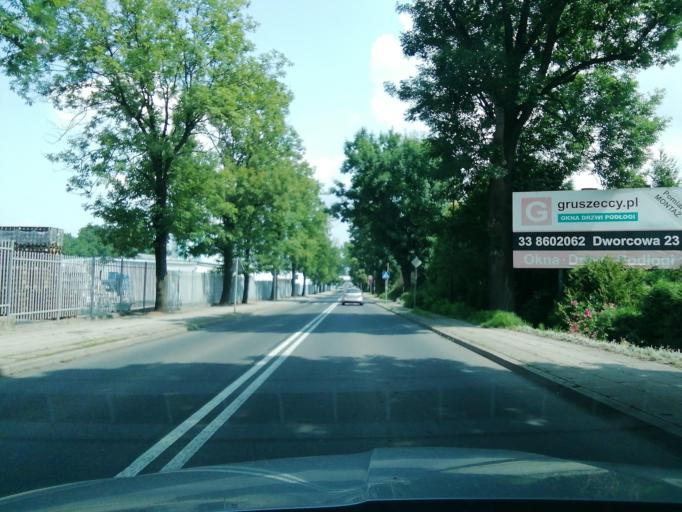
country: PL
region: Silesian Voivodeship
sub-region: Powiat zywiecki
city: Wieprz
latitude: 49.6594
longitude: 19.1726
